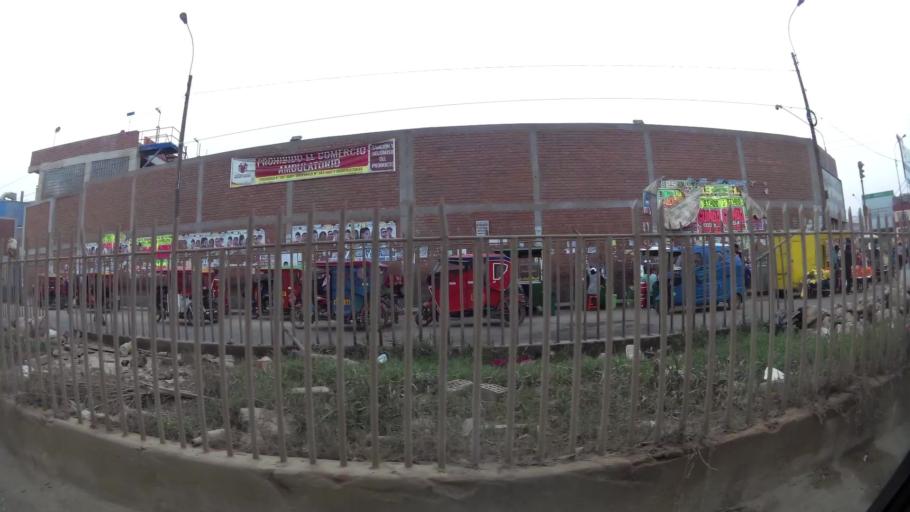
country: PE
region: Lima
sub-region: Lima
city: Carabayllo
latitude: -11.8648
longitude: -77.0739
